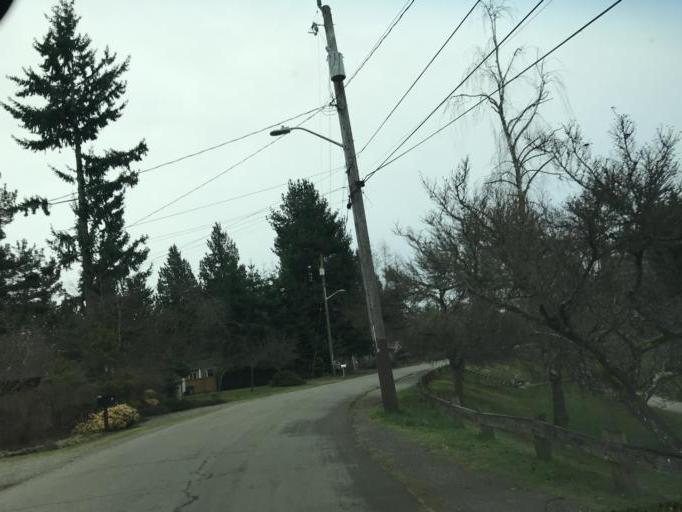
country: US
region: Washington
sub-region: King County
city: Lake Forest Park
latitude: 47.7061
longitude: -122.3076
